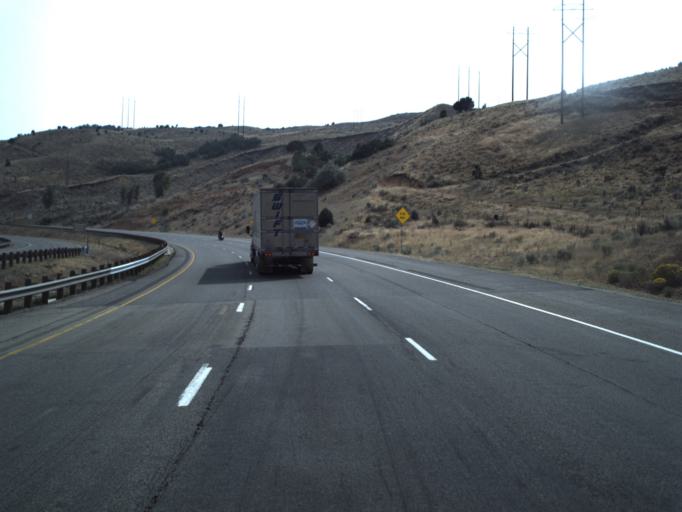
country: US
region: Utah
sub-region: Summit County
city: Coalville
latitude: 40.9679
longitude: -111.4391
